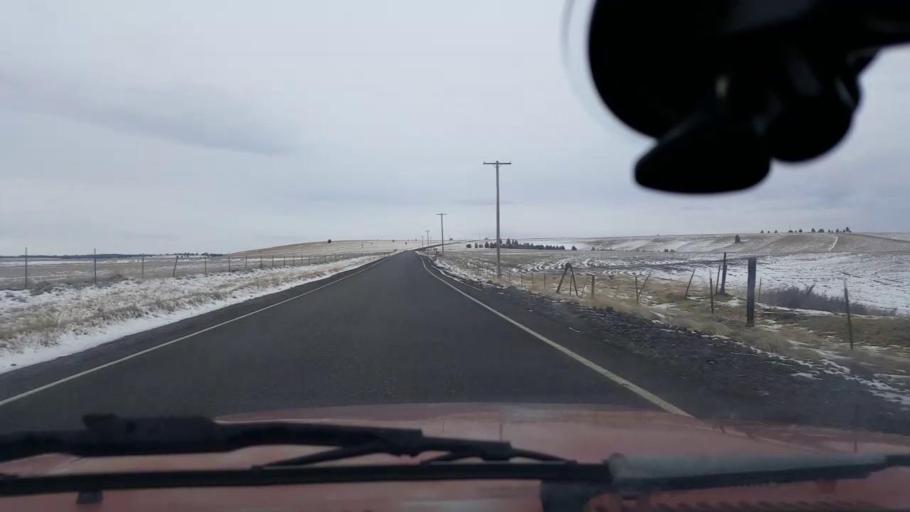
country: US
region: Washington
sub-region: Garfield County
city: Pomeroy
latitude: 46.3201
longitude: -117.3923
